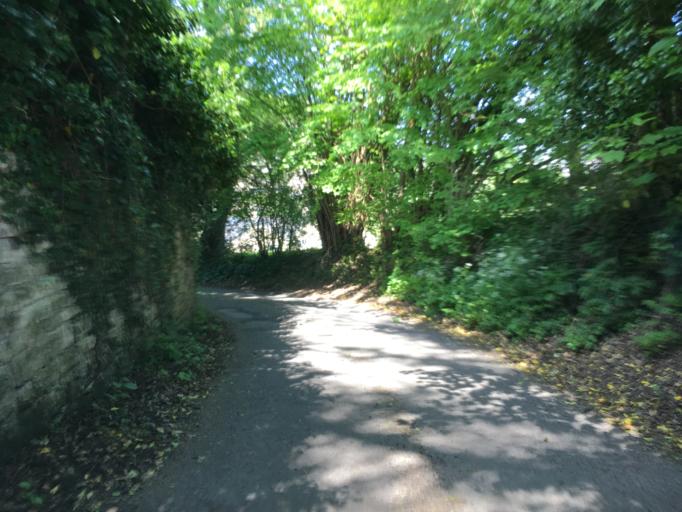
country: GB
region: England
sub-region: Gloucestershire
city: Stroud
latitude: 51.7298
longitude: -2.2089
